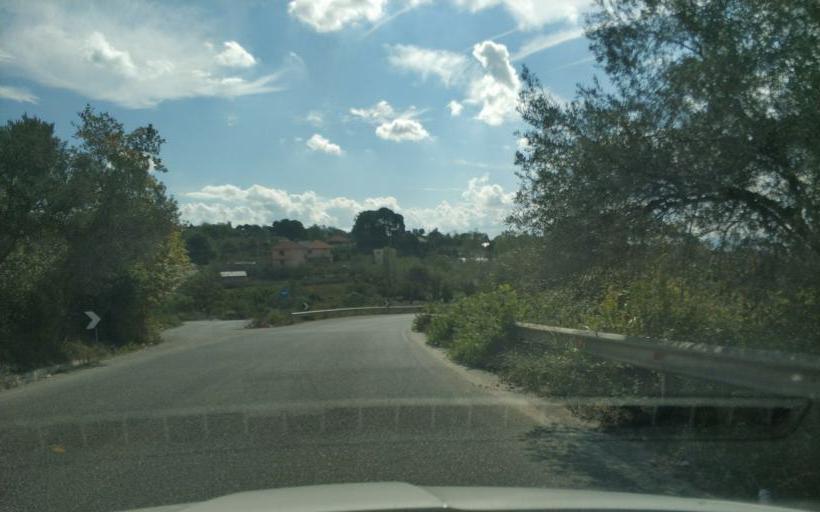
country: AL
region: Durres
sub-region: Rrethi i Krujes
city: Kruje
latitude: 41.4830
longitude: 19.7657
